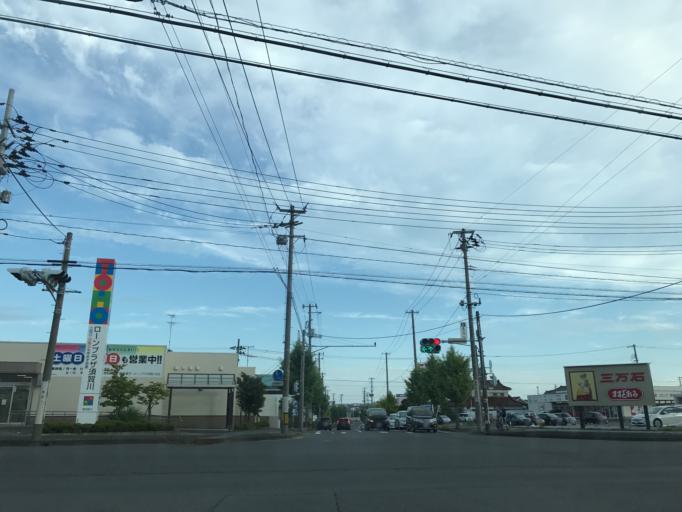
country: JP
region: Fukushima
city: Sukagawa
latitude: 37.2975
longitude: 140.3618
